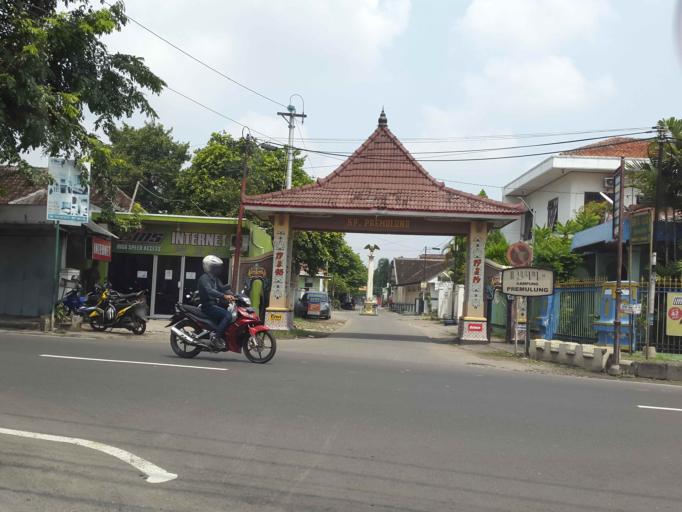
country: ID
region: Central Java
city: Surakarta
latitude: -7.5661
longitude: 110.7936
